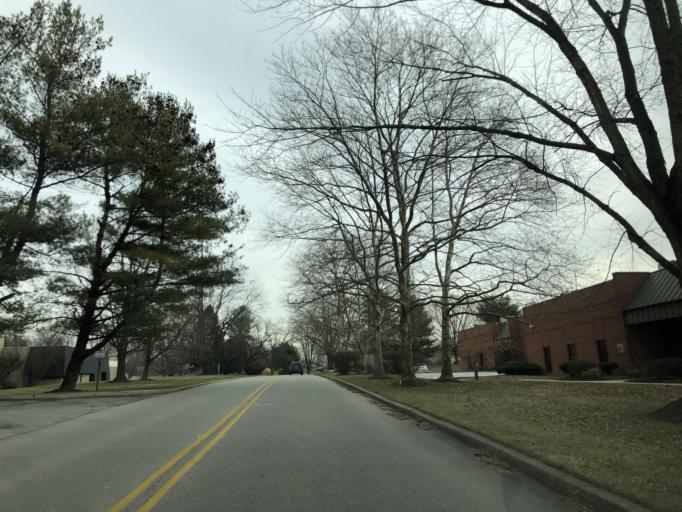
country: US
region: Pennsylvania
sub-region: Chester County
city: Exton
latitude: 40.0224
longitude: -75.6411
